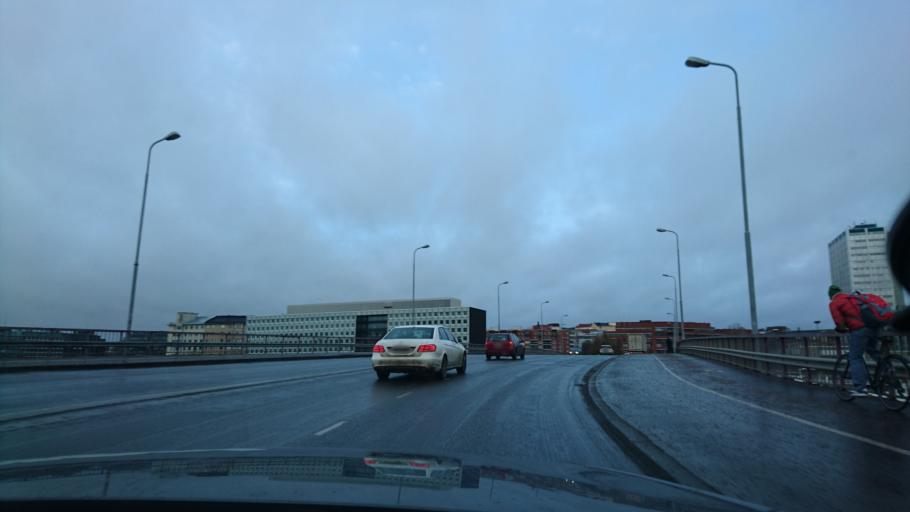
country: FI
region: Uusimaa
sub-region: Helsinki
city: Helsinki
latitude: 60.1766
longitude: 24.9576
